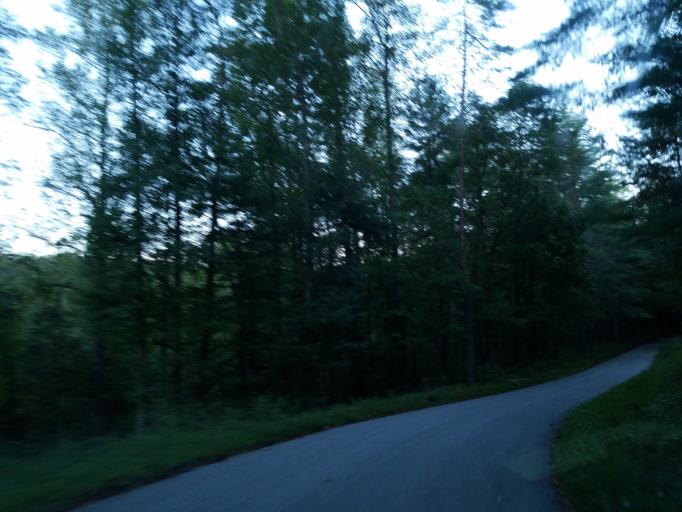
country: US
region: Georgia
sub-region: Dawson County
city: Dawsonville
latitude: 34.5719
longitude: -84.1558
